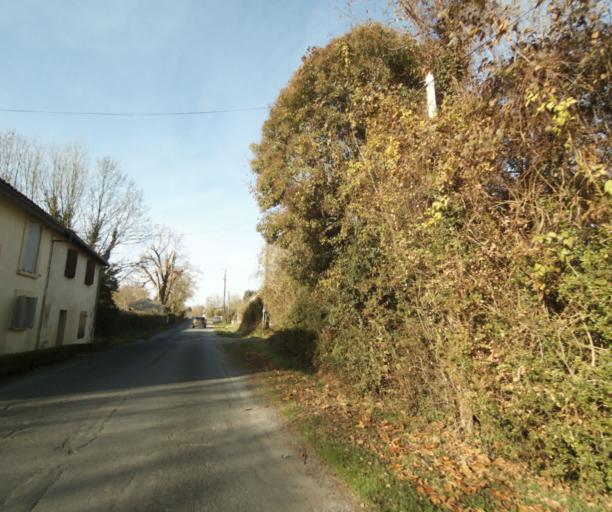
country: FR
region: Poitou-Charentes
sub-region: Departement de la Charente-Maritime
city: Chaniers
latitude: 45.7129
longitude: -0.5464
